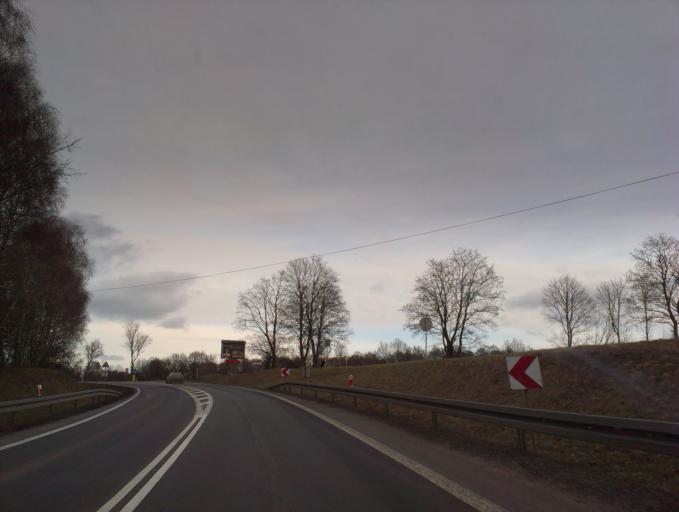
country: PL
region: Masovian Voivodeship
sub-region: Powiat sierpecki
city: Sierpc
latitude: 52.8683
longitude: 19.6327
